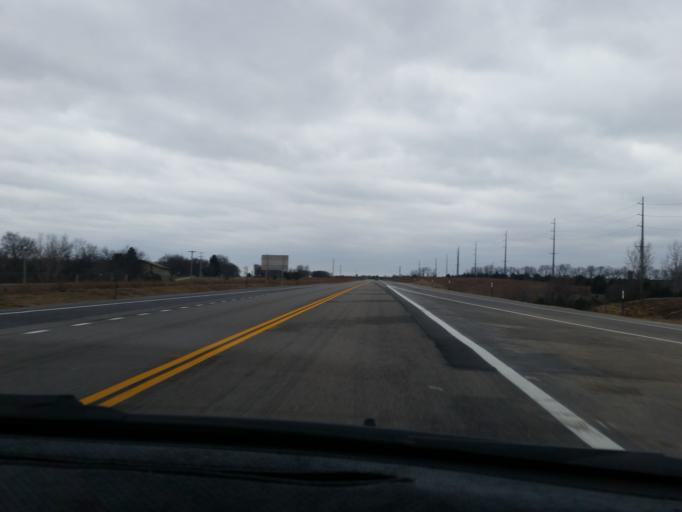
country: US
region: Kansas
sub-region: Douglas County
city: Lawrence
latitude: 38.9556
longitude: -95.3351
